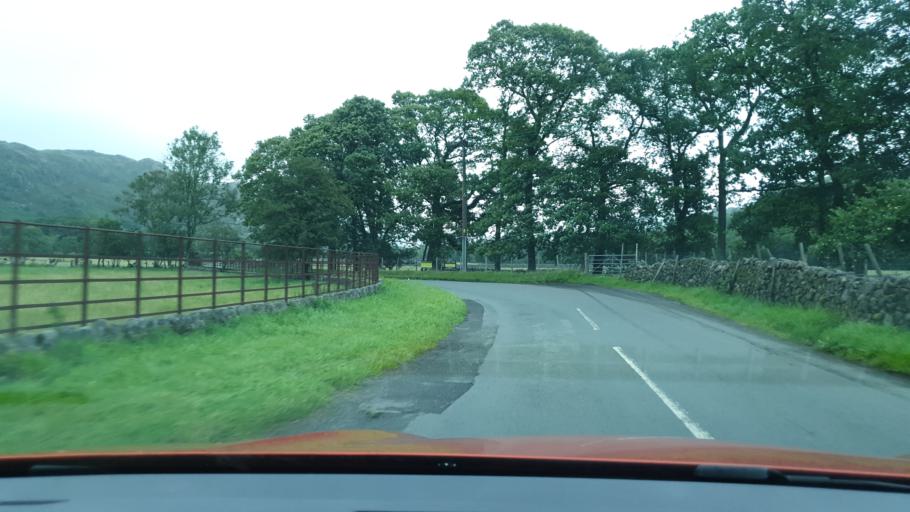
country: GB
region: England
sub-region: Cumbria
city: Seascale
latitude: 54.3868
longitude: -3.3115
